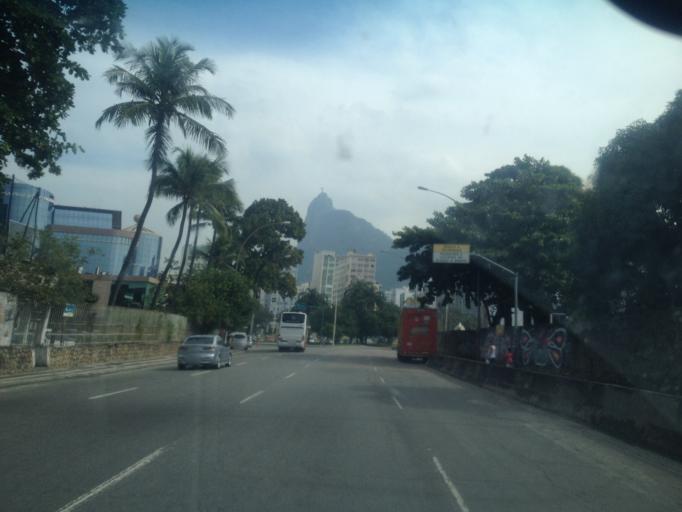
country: BR
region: Rio de Janeiro
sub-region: Rio De Janeiro
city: Rio de Janeiro
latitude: -22.9495
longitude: -43.1788
